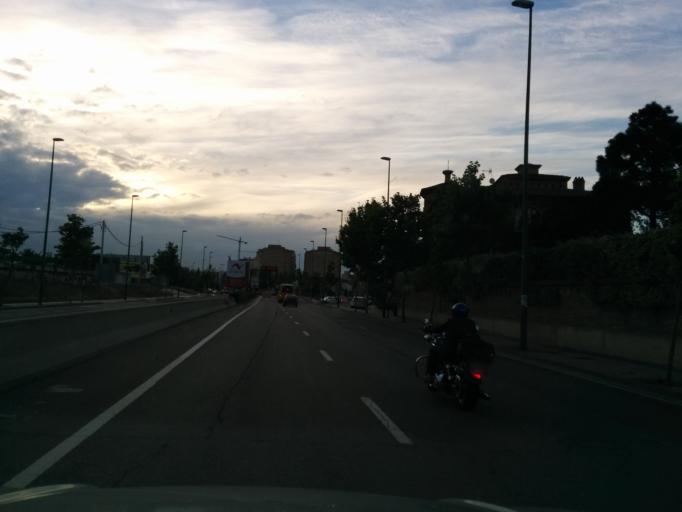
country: ES
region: Aragon
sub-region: Provincia de Zaragoza
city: Zaragoza
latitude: 41.6325
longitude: -0.8595
